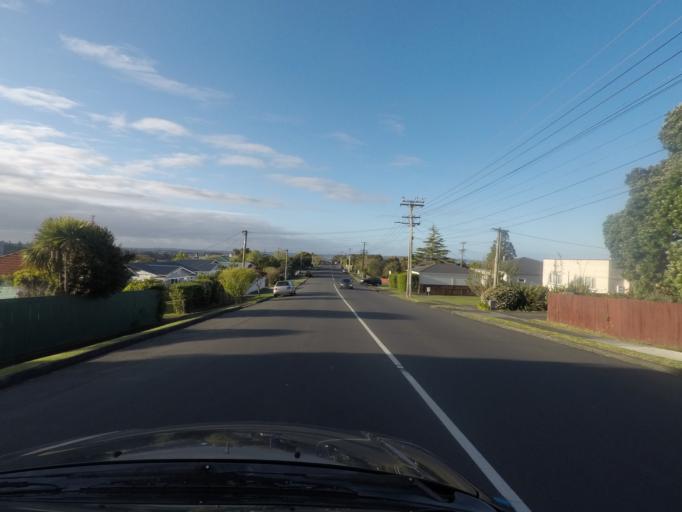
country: NZ
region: Auckland
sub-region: Auckland
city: Waitakere
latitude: -36.9160
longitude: 174.6579
